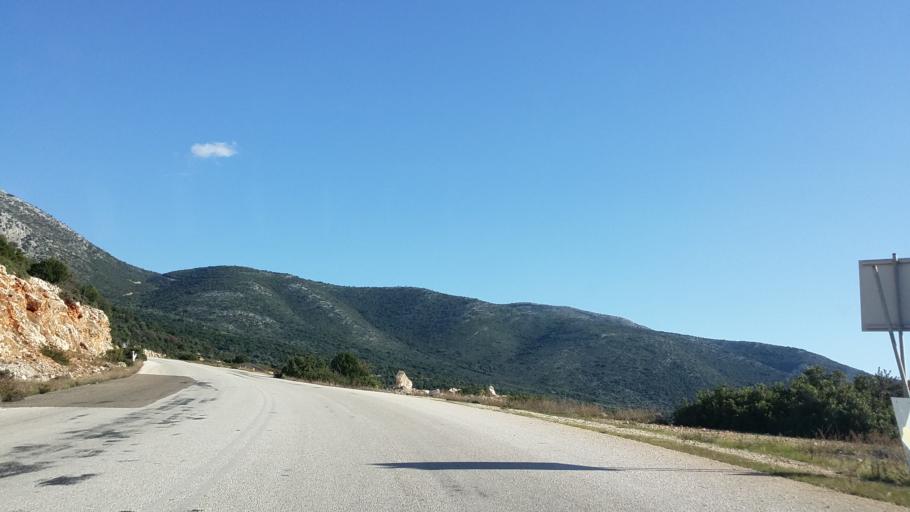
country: GR
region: West Greece
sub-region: Nomos Aitolias kai Akarnanias
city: Astakos
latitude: 38.5419
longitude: 21.0212
